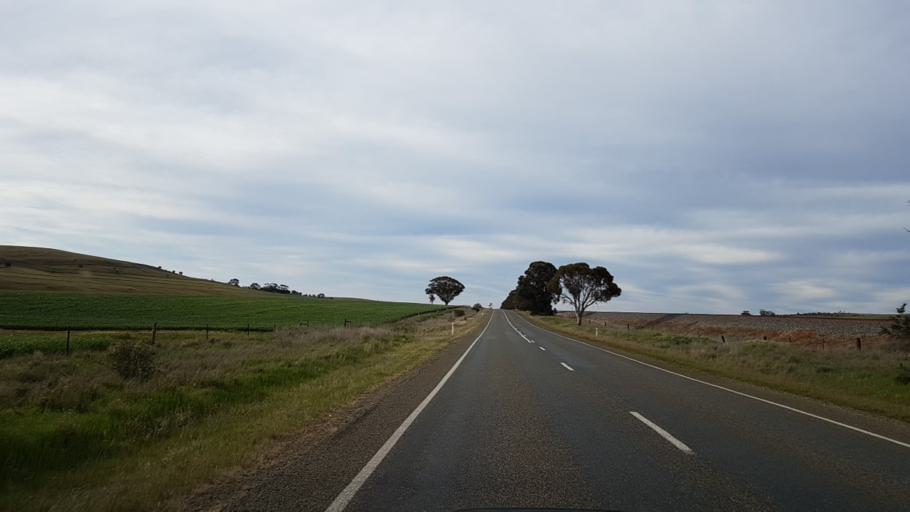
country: AU
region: South Australia
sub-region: Northern Areas
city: Jamestown
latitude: -33.1357
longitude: 138.6171
